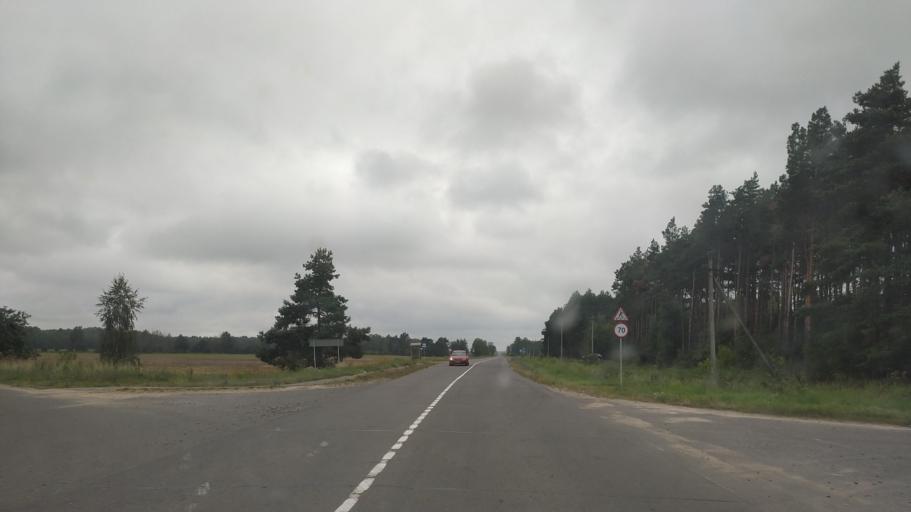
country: BY
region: Brest
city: Byaroza
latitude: 52.5573
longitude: 24.9153
